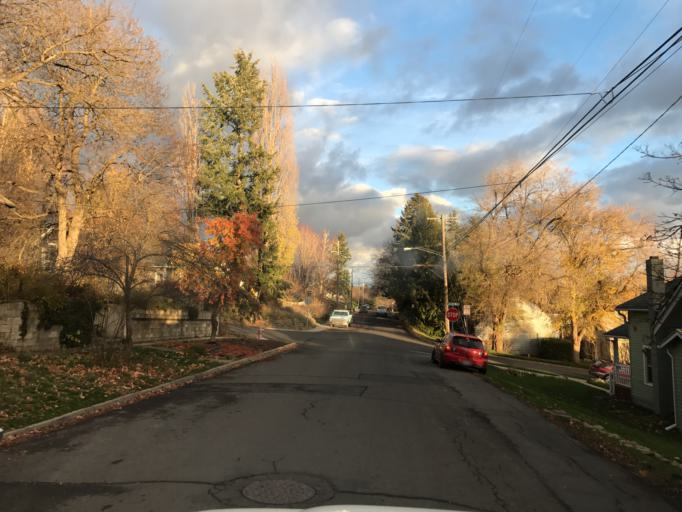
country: US
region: Idaho
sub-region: Latah County
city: Moscow
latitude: 46.7360
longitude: -117.0099
